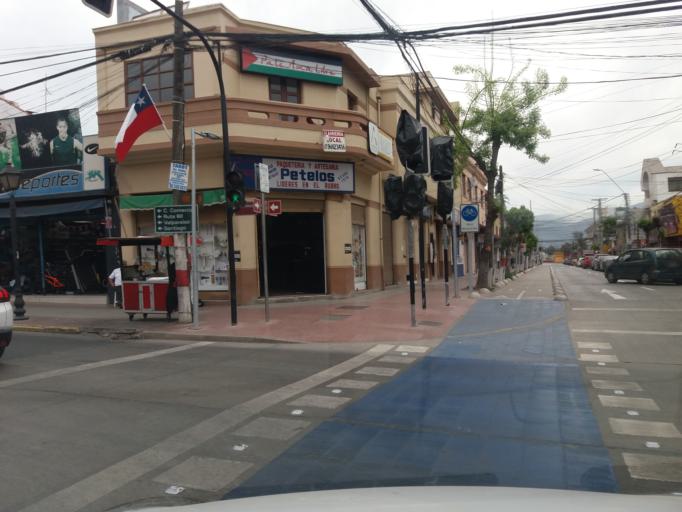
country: CL
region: Valparaiso
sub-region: Provincia de Quillota
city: Hacienda La Calera
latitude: -32.7882
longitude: -71.1896
